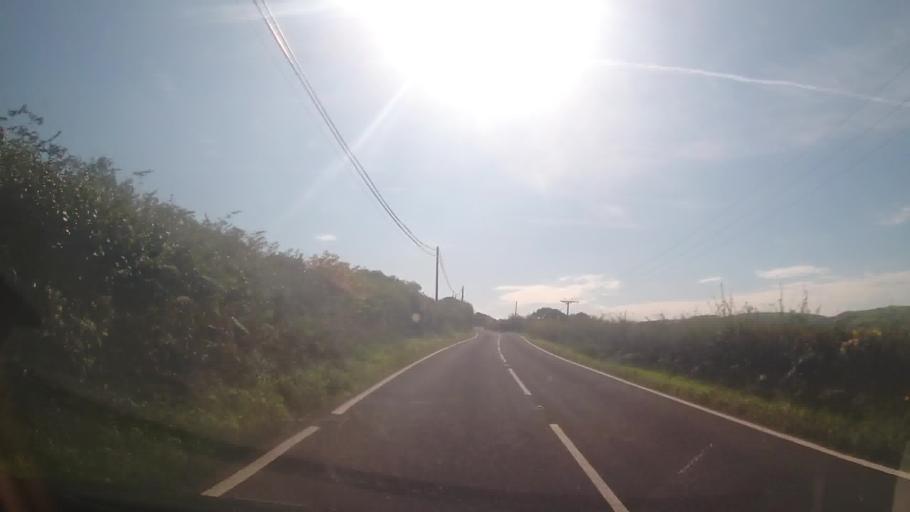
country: GB
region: Wales
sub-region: Sir Powys
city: Mochdre
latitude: 52.4930
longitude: -3.3395
